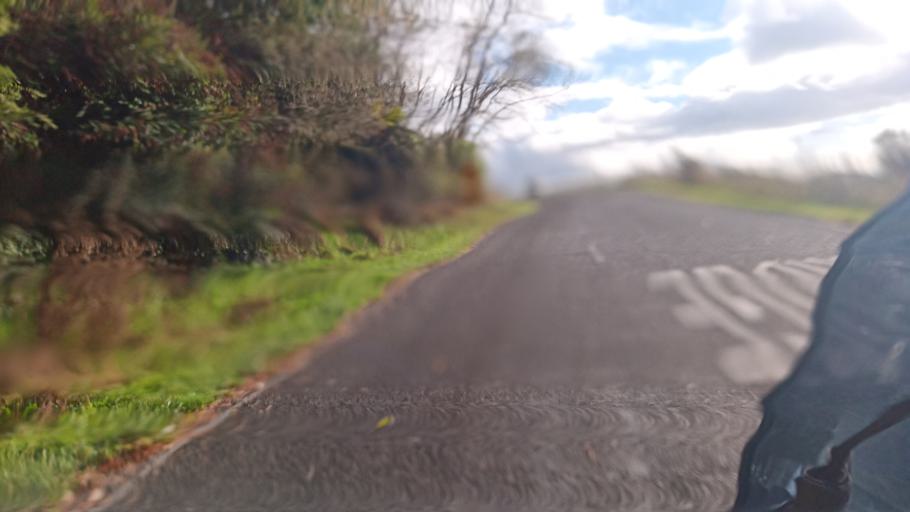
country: NZ
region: Gisborne
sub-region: Gisborne District
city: Gisborne
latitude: -38.5554
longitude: 177.6989
